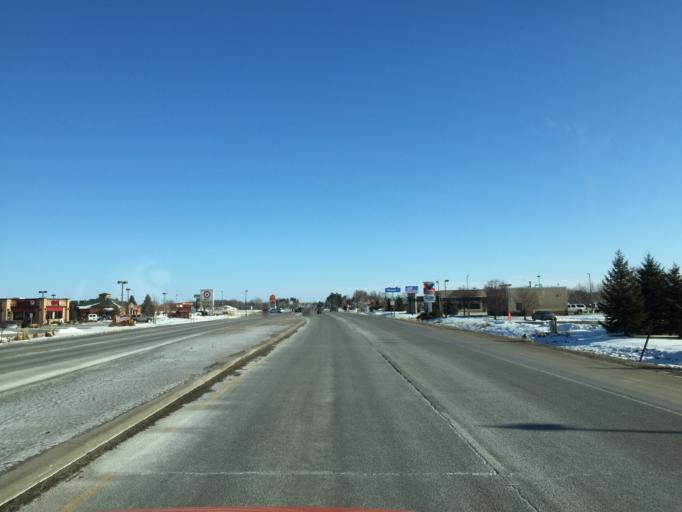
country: US
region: Minnesota
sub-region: Isanti County
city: Cambridge
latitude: 45.5727
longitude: -93.2014
